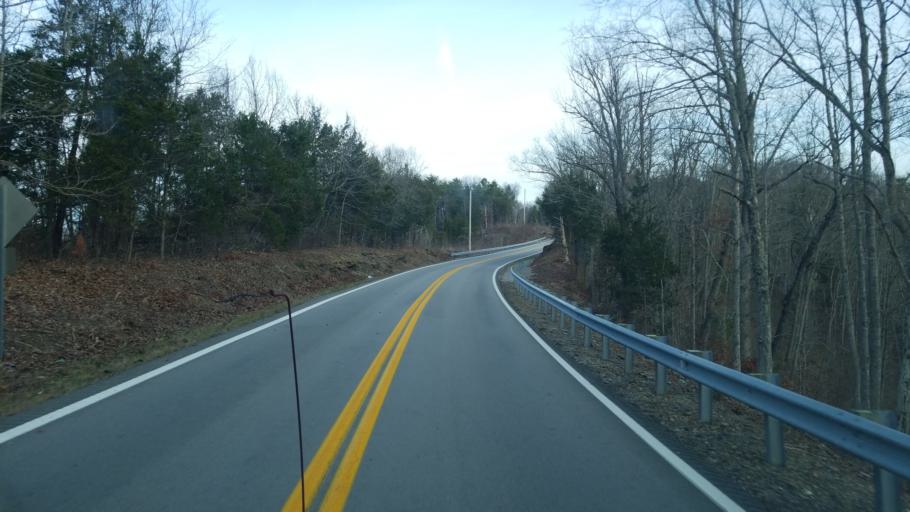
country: US
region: Kentucky
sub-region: Clinton County
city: Albany
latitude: 36.8496
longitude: -85.1614
